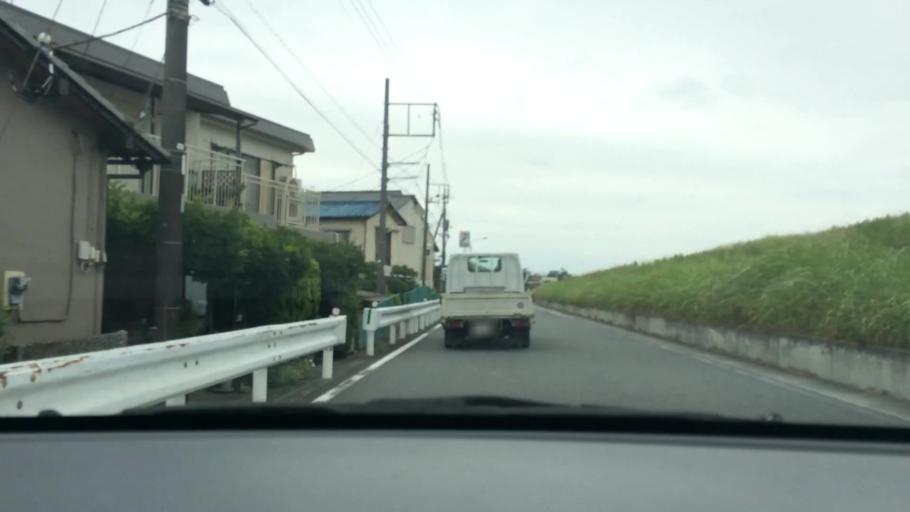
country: JP
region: Chiba
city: Matsudo
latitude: 35.7905
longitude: 139.8870
